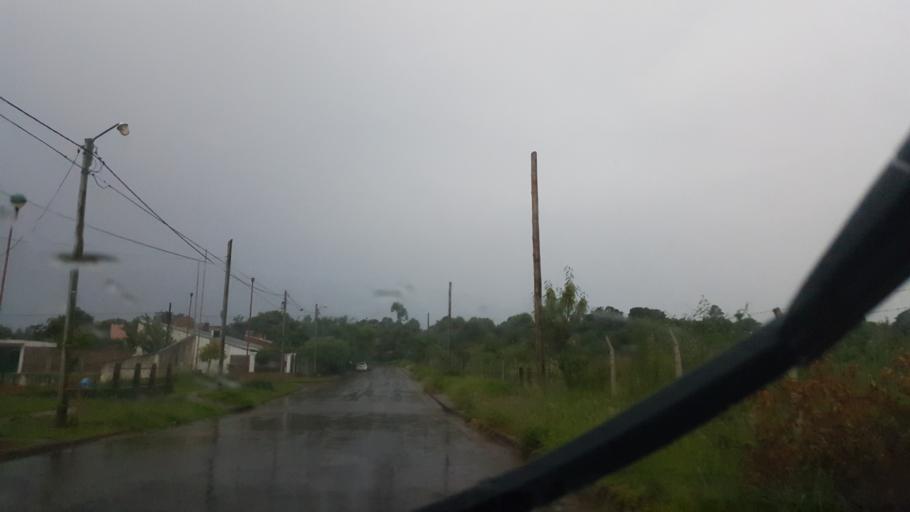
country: AR
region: Misiones
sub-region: Departamento de Capital
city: Posadas
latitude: -27.4121
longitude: -55.9442
